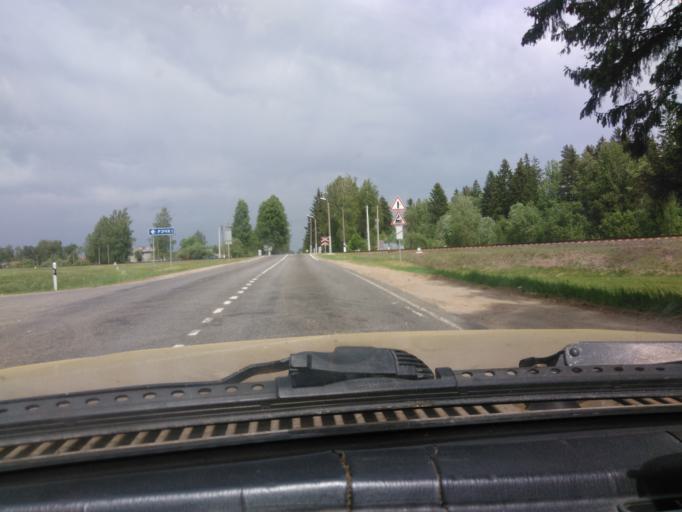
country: BY
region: Mogilev
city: Palykavichy Pyershyya
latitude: 53.9864
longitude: 30.3181
